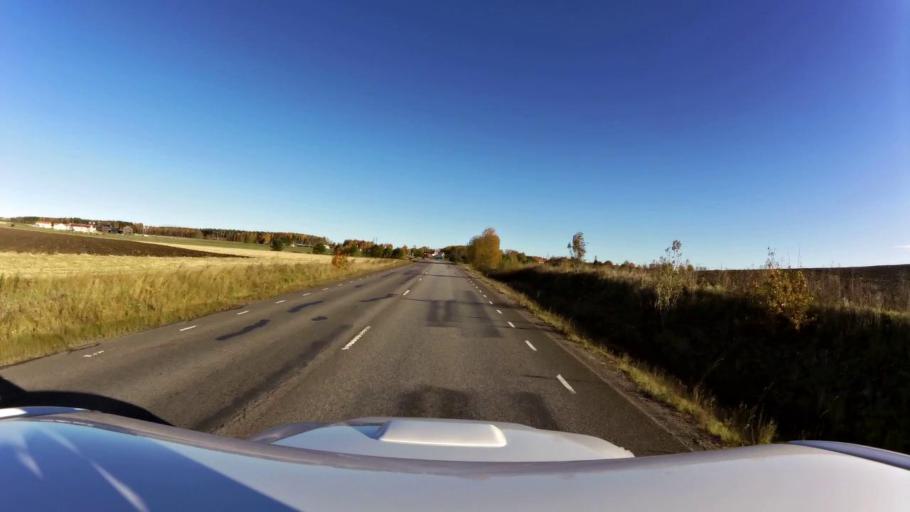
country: SE
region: OEstergoetland
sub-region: Linkopings Kommun
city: Ljungsbro
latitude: 58.4844
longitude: 15.4932
